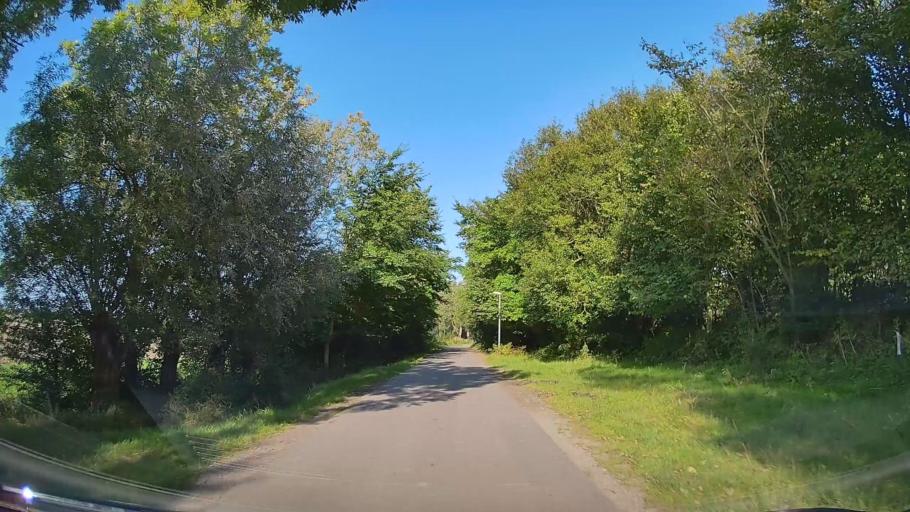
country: DE
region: Lower Saxony
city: Padingbuttel
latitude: 53.7071
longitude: 8.5044
